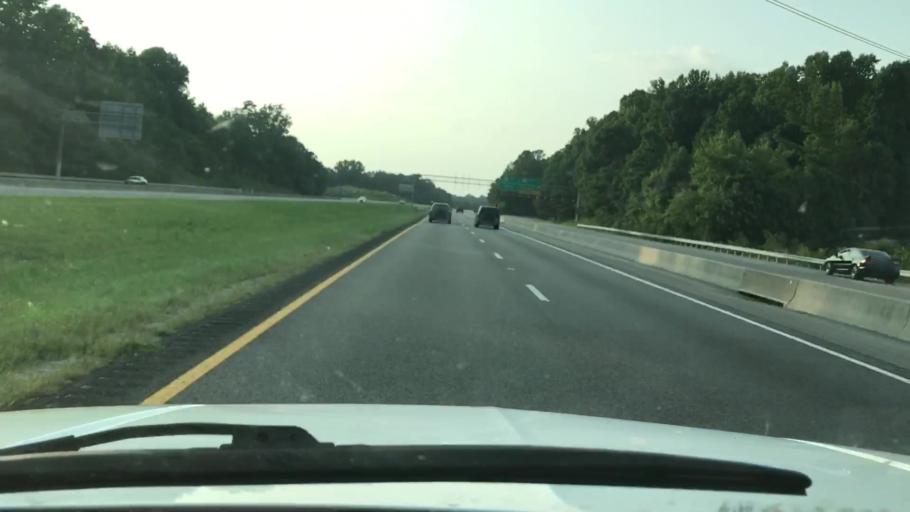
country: US
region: Virginia
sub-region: Chesterfield County
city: Brandermill
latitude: 37.4190
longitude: -77.6255
